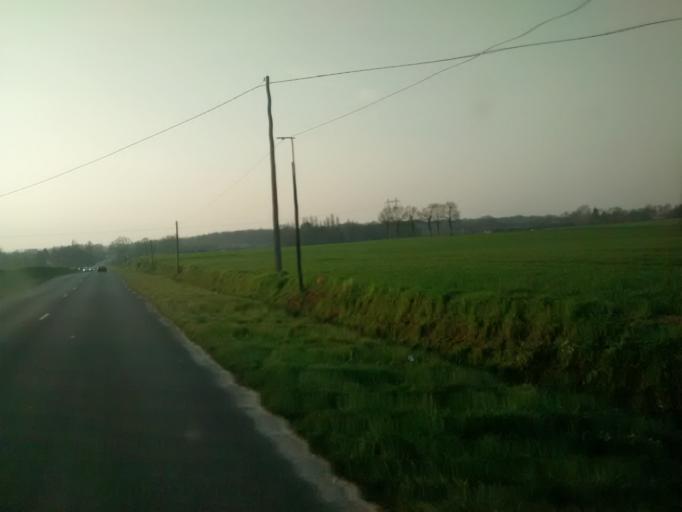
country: FR
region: Brittany
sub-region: Departement d'Ille-et-Vilaine
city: Chavagne
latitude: 48.0634
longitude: -1.8123
